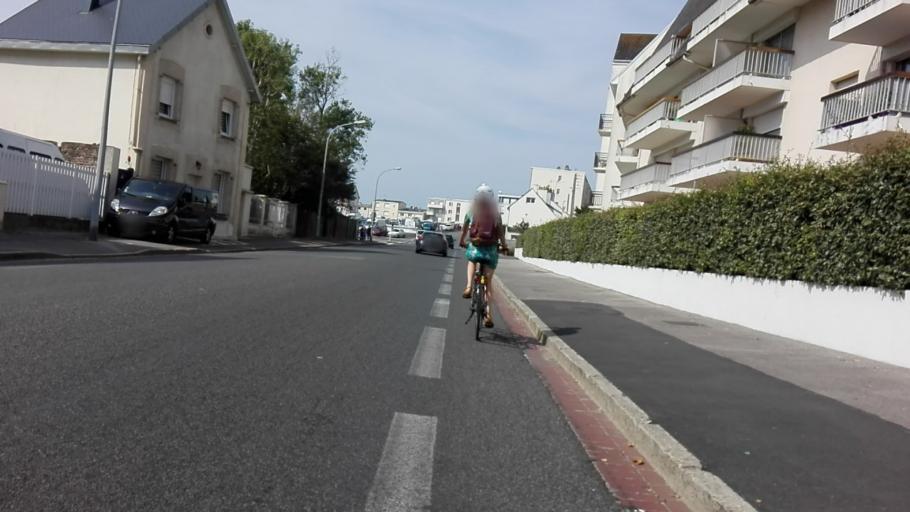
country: FR
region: Nord-Pas-de-Calais
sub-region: Departement du Pas-de-Calais
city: Berck-Plage
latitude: 50.4108
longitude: 1.5669
